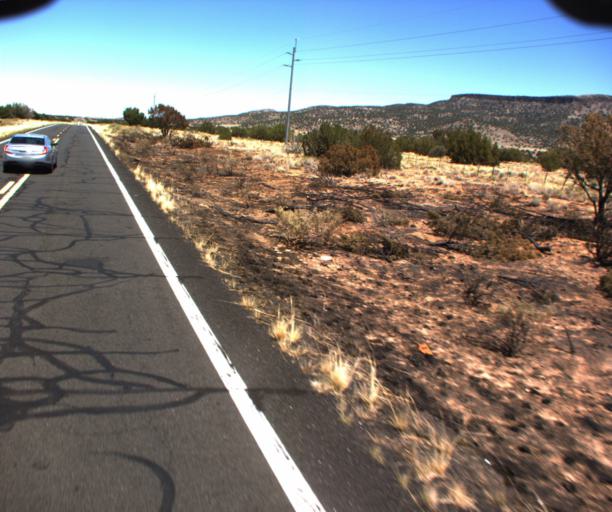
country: US
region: Arizona
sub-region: Coconino County
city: LeChee
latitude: 34.8412
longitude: -110.9388
